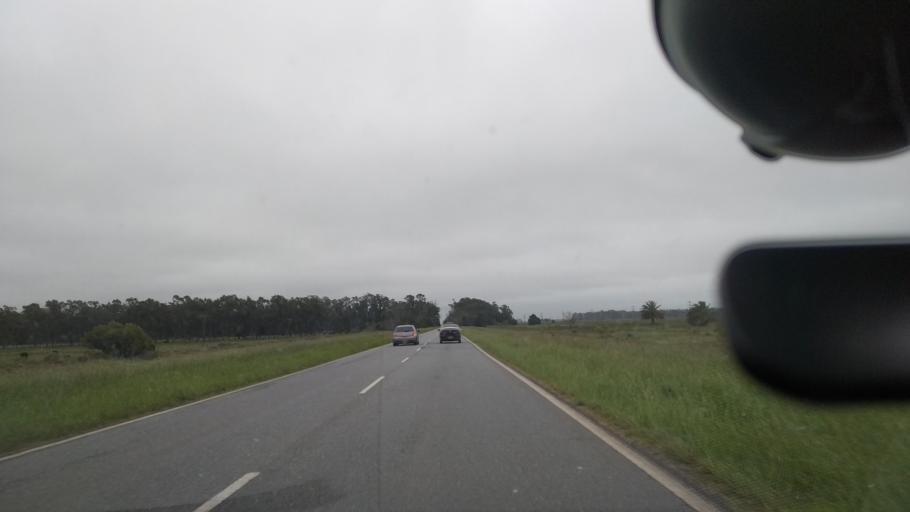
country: AR
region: Buenos Aires
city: Veronica
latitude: -35.3218
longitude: -57.4756
